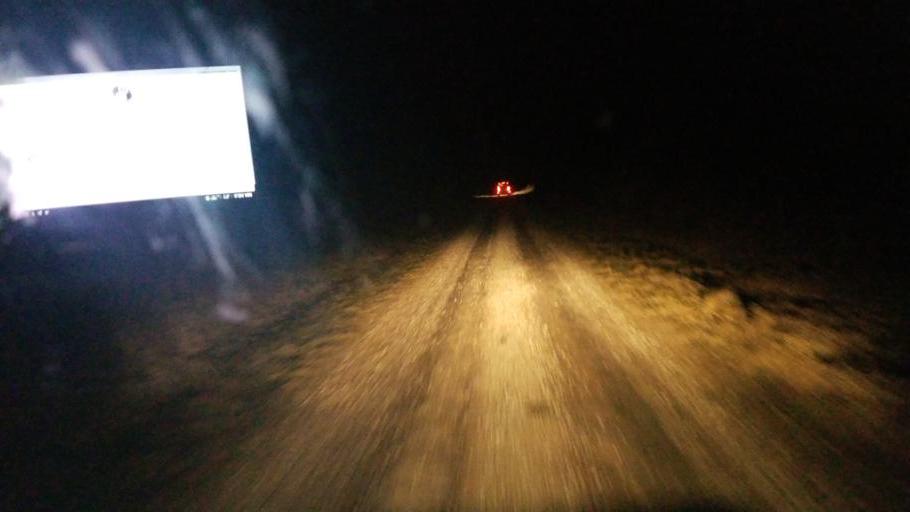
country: US
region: Illinois
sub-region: Warren County
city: Monmouth
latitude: 40.7627
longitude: -90.7601
